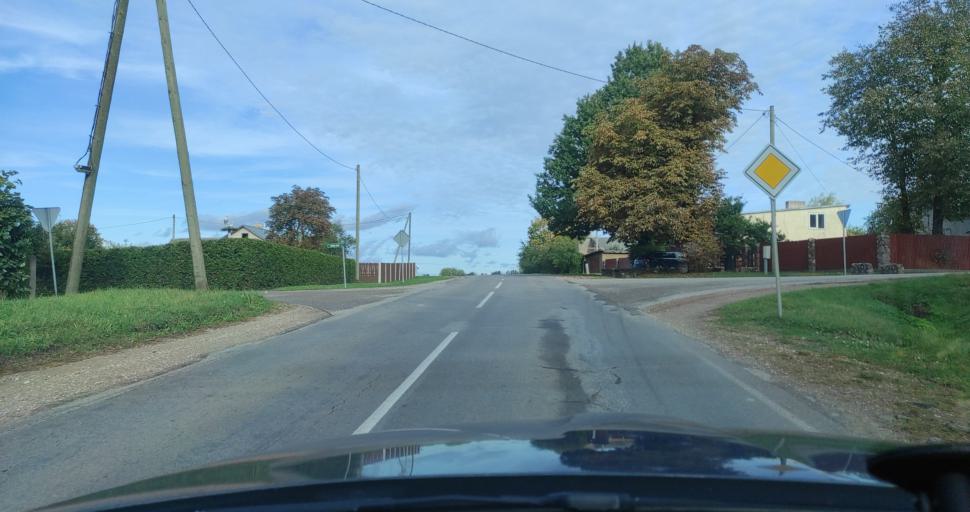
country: LV
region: Jaunpils
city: Jaunpils
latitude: 56.7327
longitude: 23.0138
